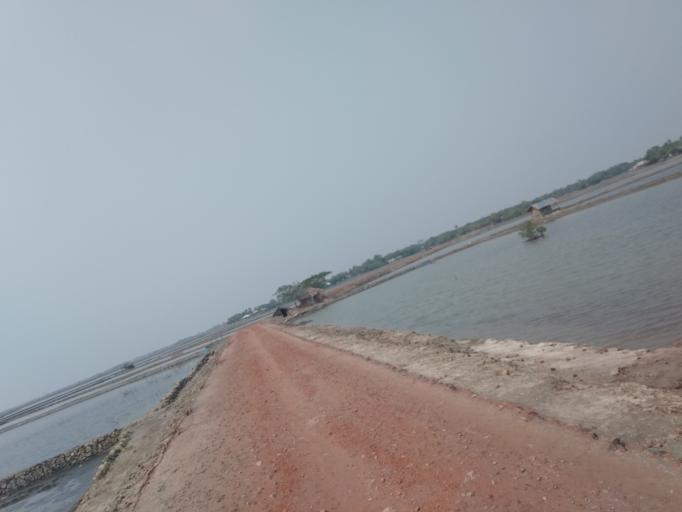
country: IN
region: West Bengal
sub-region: North 24 Parganas
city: Taki
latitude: 22.2922
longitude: 89.2711
